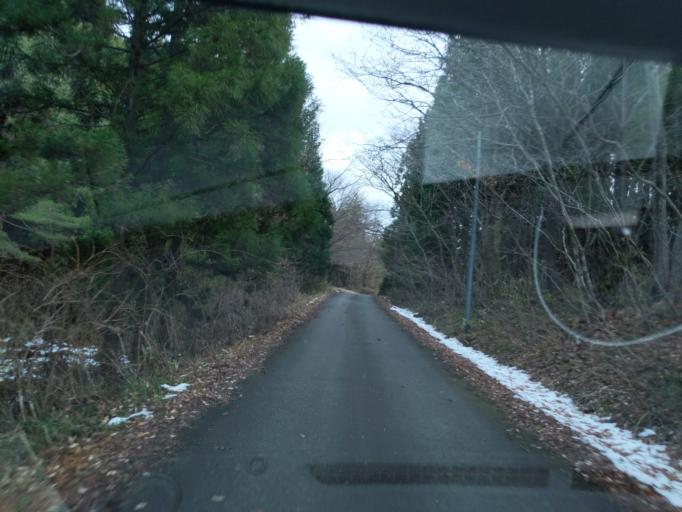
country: JP
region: Iwate
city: Ichinoseki
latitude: 38.9761
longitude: 141.0419
